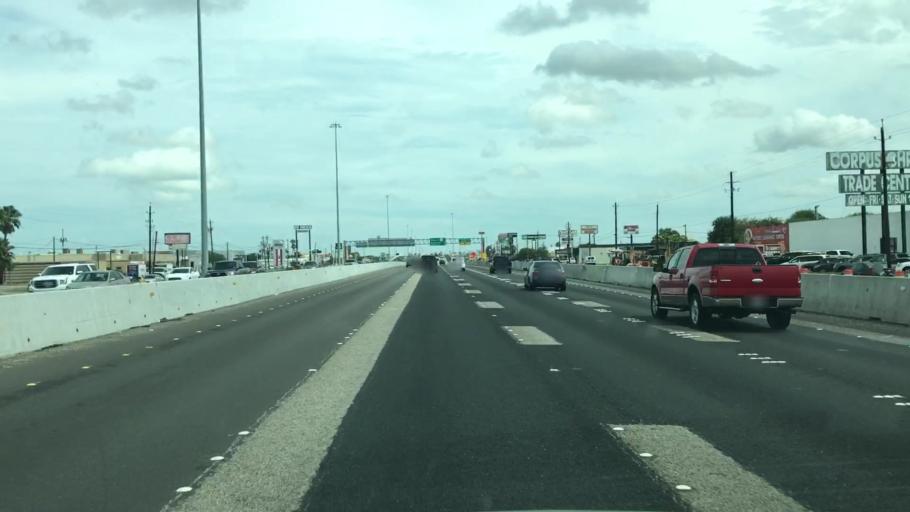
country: US
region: Texas
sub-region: Nueces County
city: Corpus Christi
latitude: 27.7317
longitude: -97.4195
